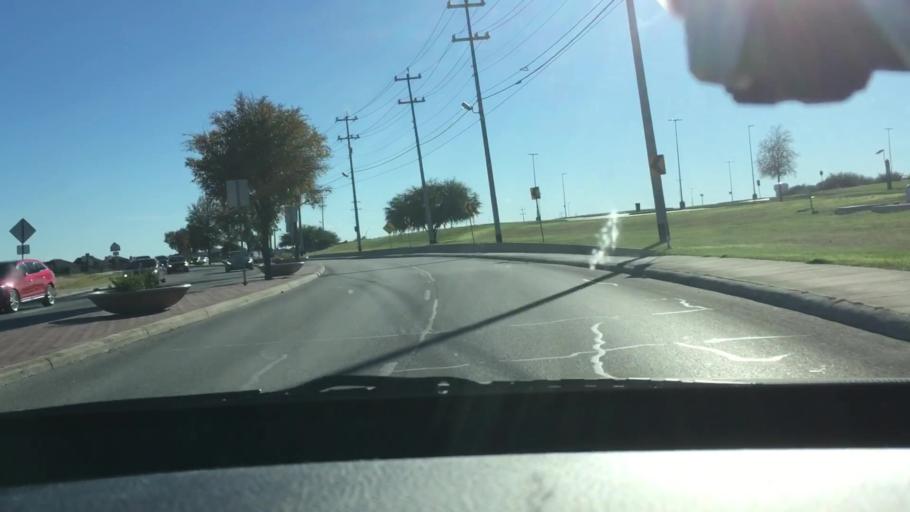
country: US
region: Texas
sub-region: Bexar County
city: Converse
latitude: 29.5432
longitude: -98.3219
